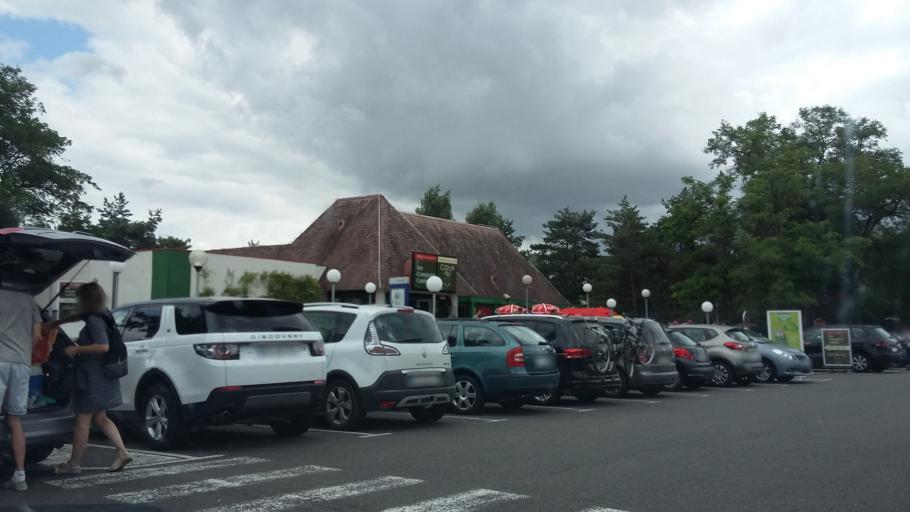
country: FR
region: Poitou-Charentes
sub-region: Departement de la Vienne
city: Antran
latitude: 46.9061
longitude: 0.5234
